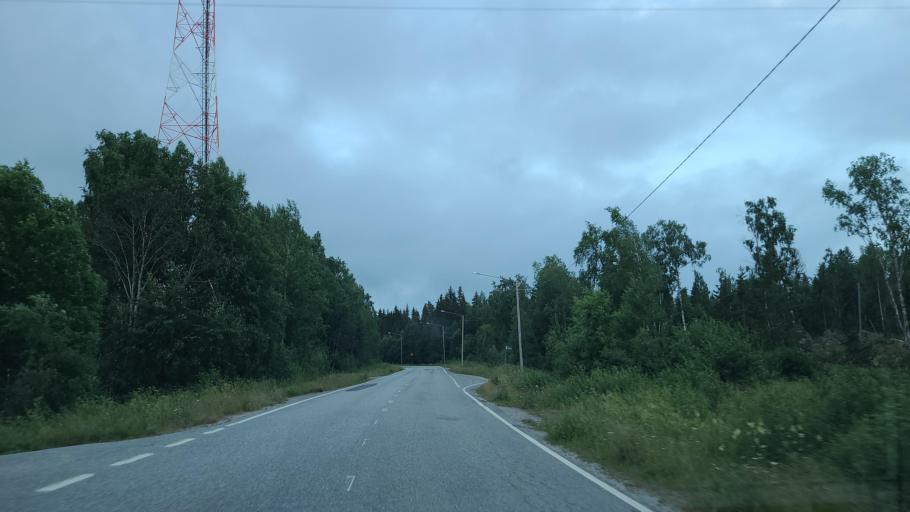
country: FI
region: Ostrobothnia
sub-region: Vaasa
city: Replot
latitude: 63.2873
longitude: 21.1165
